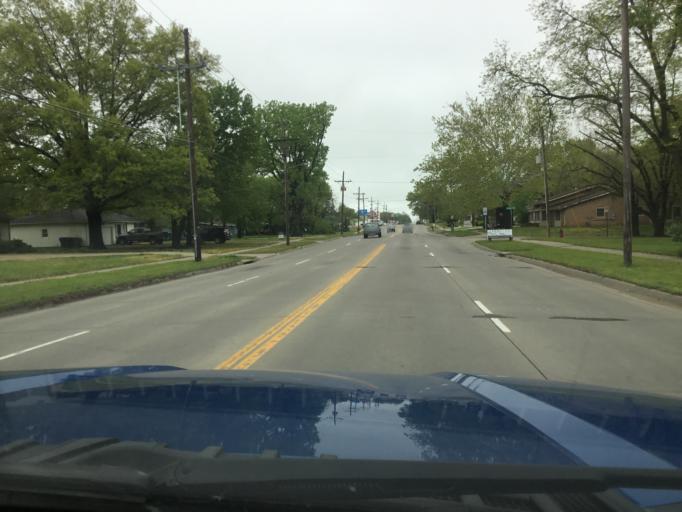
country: US
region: Kansas
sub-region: Shawnee County
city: Topeka
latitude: 39.0294
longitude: -95.7340
